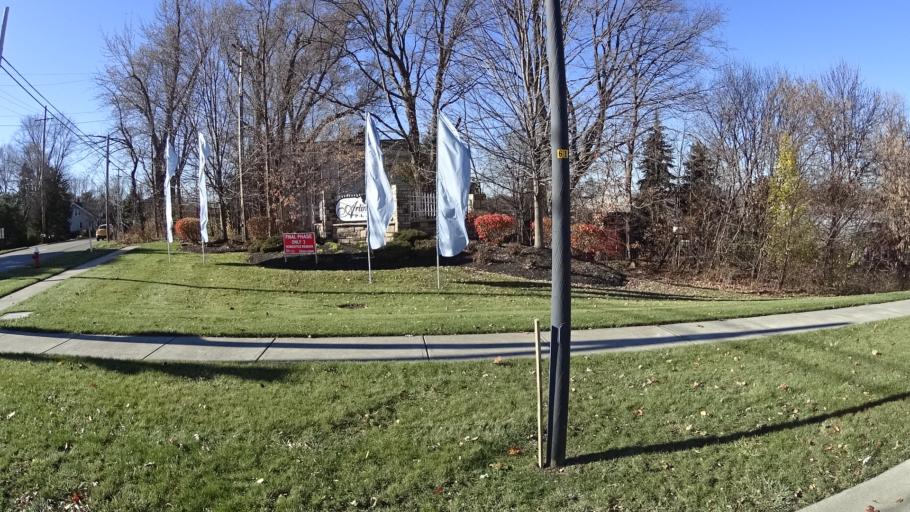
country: US
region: Ohio
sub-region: Lorain County
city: Avon
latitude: 41.4331
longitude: -82.0624
